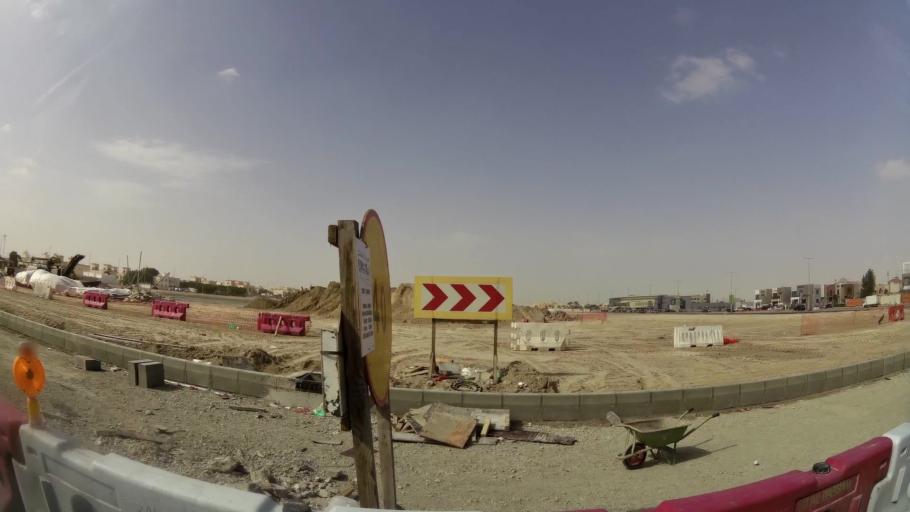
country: AE
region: Abu Dhabi
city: Abu Dhabi
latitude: 24.4243
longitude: 54.5644
